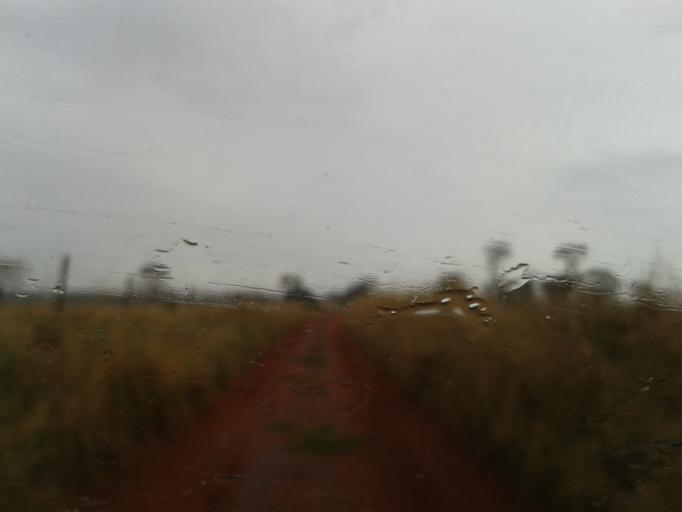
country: BR
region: Minas Gerais
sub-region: Campina Verde
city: Campina Verde
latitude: -19.3519
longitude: -49.5497
